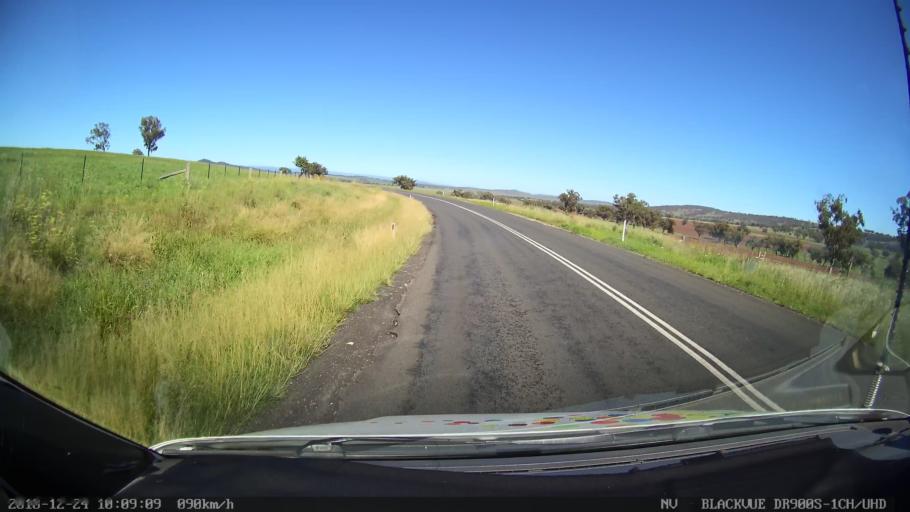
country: AU
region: New South Wales
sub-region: Liverpool Plains
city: Quirindi
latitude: -31.6632
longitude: 150.6949
